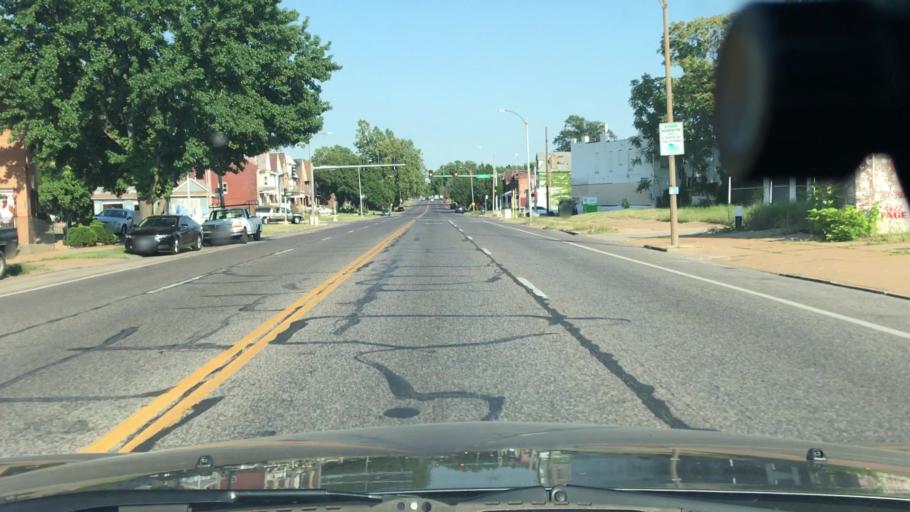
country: US
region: Missouri
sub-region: Saint Louis County
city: Hillsdale
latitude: 38.6590
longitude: -90.2573
